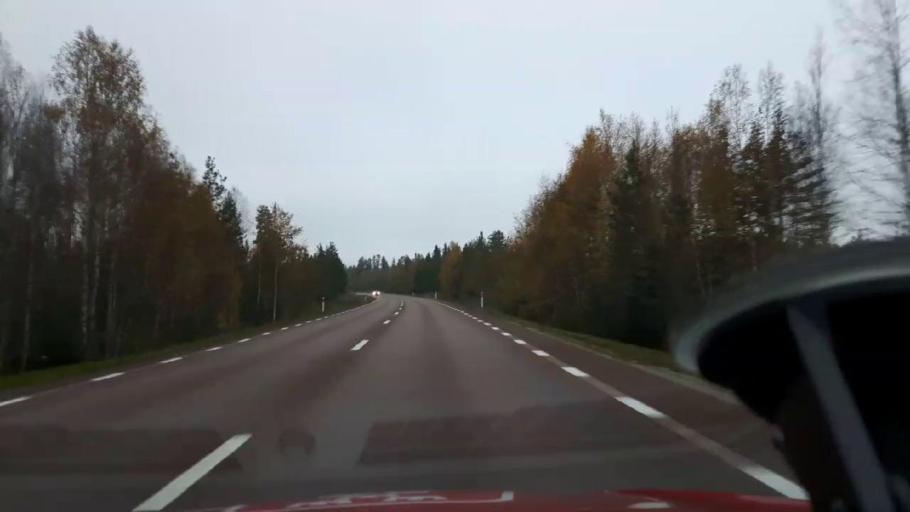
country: SE
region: Jaemtland
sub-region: Bergs Kommun
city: Hoverberg
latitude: 62.5100
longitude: 14.4496
